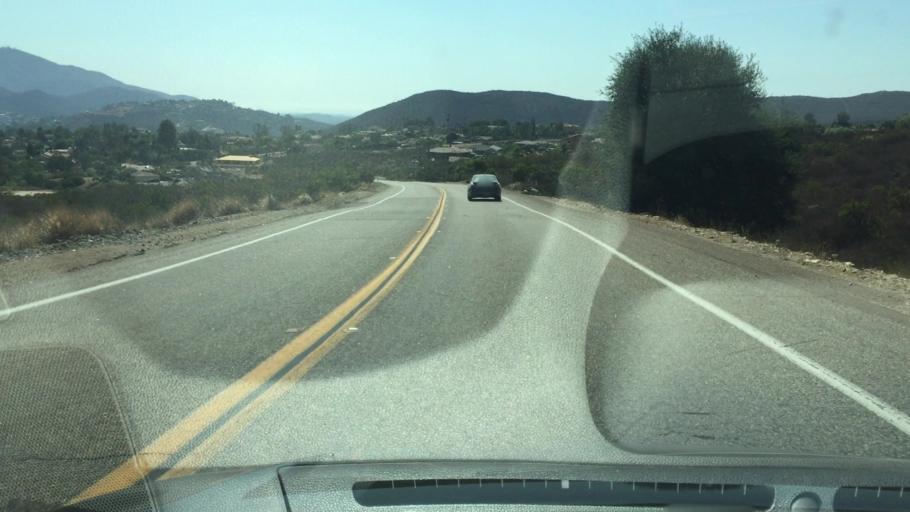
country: US
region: California
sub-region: San Diego County
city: Jamul
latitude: 32.7357
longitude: -116.8451
